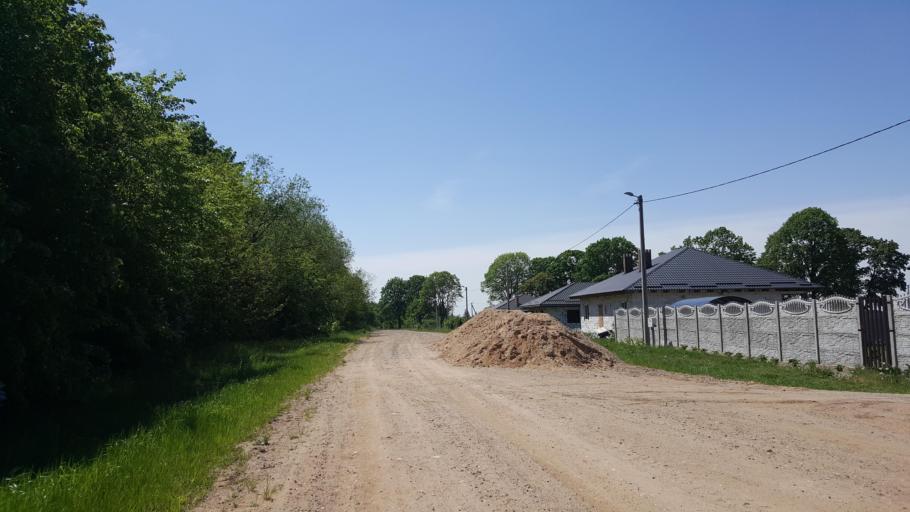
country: BY
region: Brest
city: Charnawchytsy
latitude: 52.2673
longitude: 23.7663
